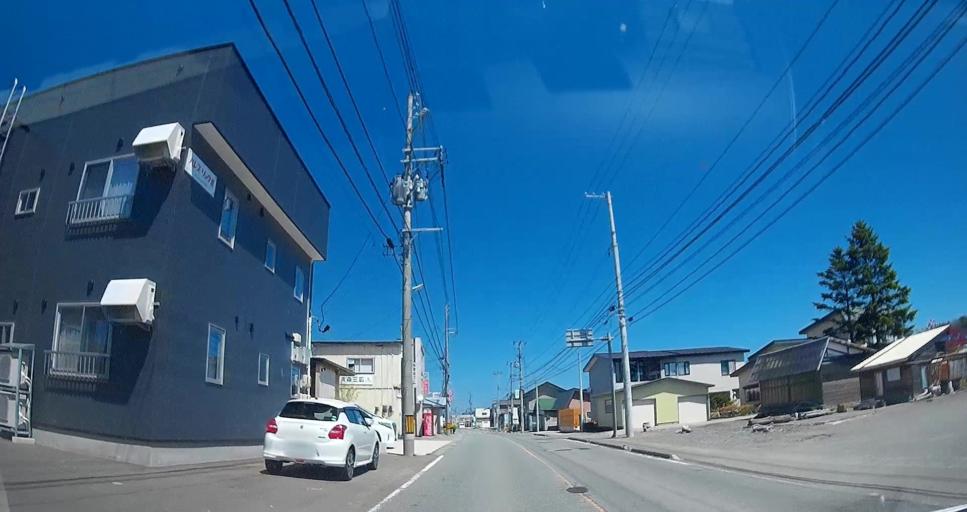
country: JP
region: Aomori
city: Misawa
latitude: 40.9639
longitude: 141.3746
